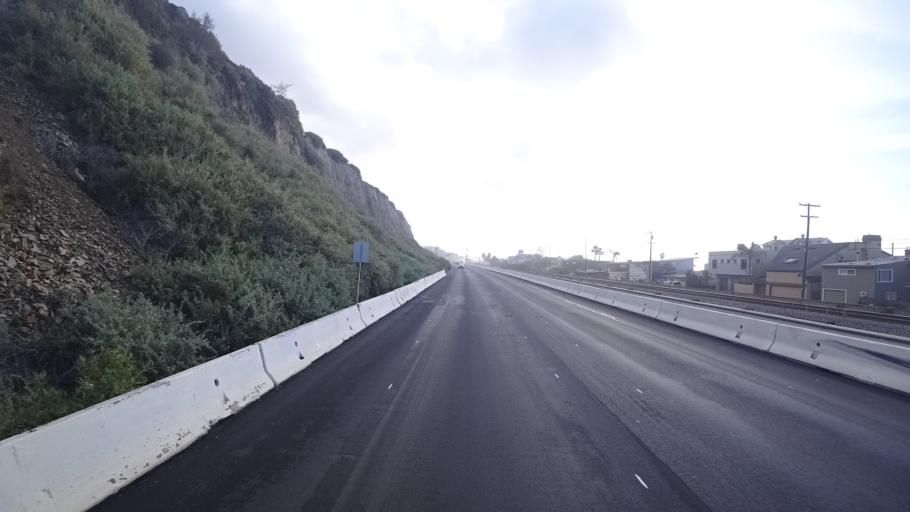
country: US
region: California
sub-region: Orange County
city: San Clemente
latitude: 33.4430
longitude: -117.6476
